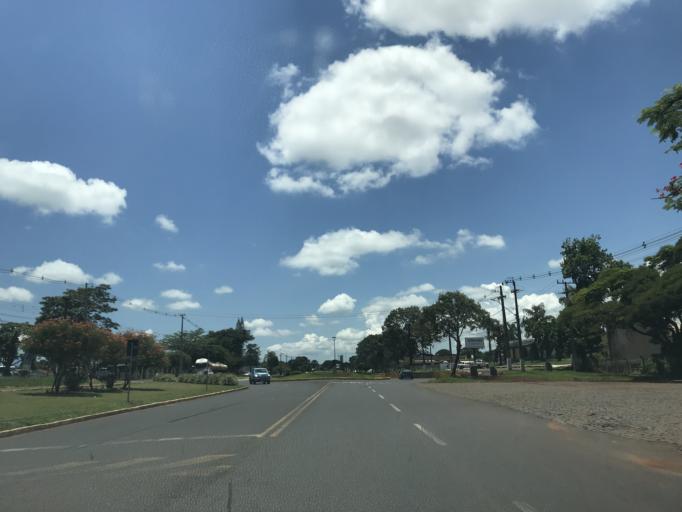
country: BR
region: Parana
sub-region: Marialva
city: Marialva
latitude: -23.4752
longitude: -51.8130
